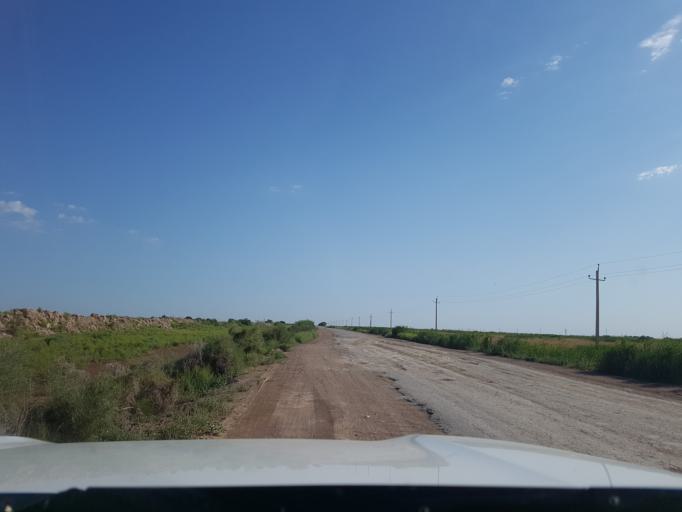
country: TM
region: Dasoguz
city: Koeneuergench
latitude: 41.9216
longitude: 58.7118
